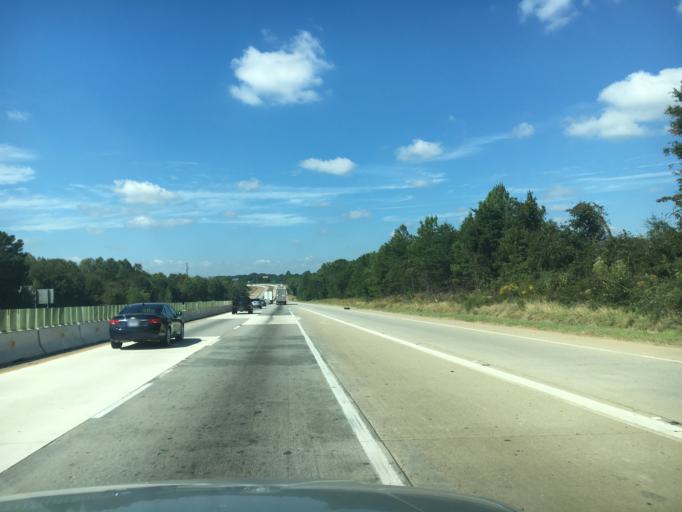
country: US
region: South Carolina
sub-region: Spartanburg County
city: Valley Falls
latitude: 35.0129
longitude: -81.9625
